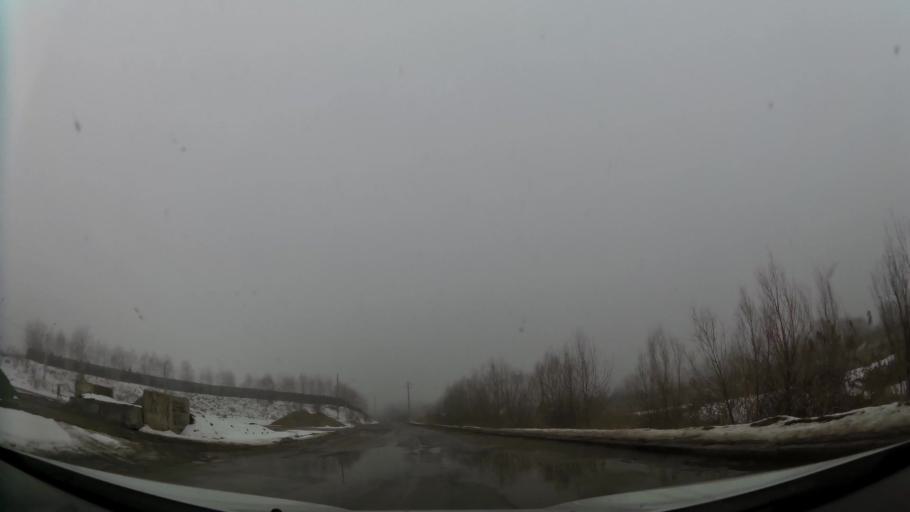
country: RO
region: Ilfov
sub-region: Comuna Chitila
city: Rudeni
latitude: 44.4663
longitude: 25.9825
